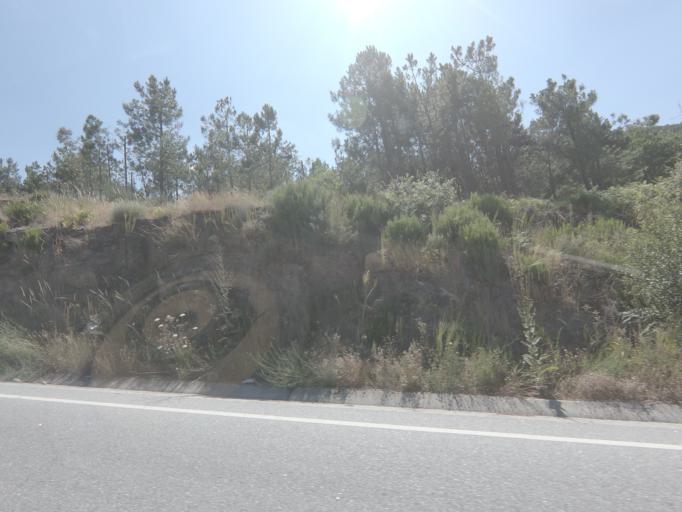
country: PT
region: Viseu
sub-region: Tarouca
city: Tarouca
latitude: 41.0025
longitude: -7.7815
